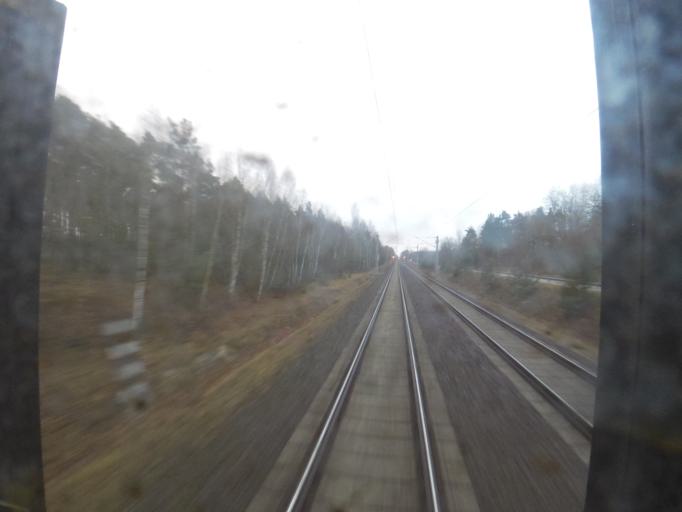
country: DE
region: Brandenburg
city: Doberlug-Kirchhain
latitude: 51.6056
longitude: 13.5648
